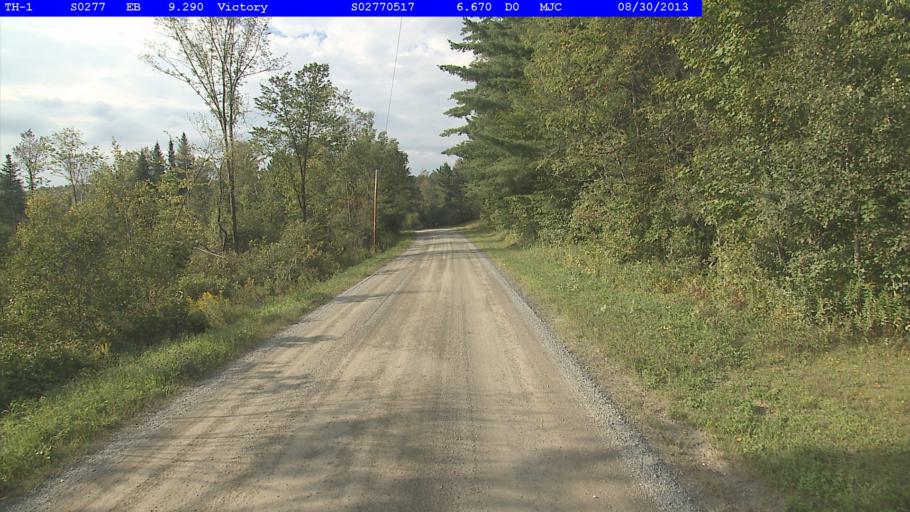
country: US
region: Vermont
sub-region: Caledonia County
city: Lyndonville
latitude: 44.5642
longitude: -71.7875
